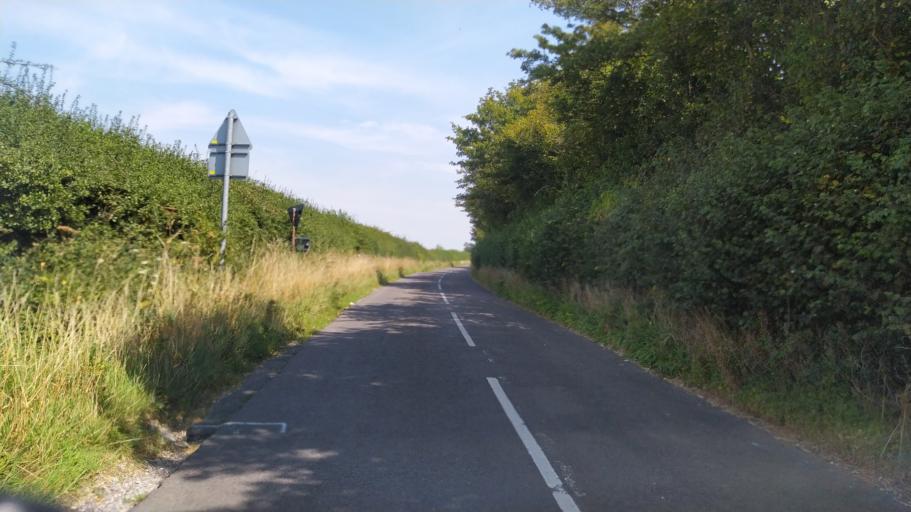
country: GB
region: England
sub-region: Hampshire
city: Cowplain
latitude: 50.9462
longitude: -1.0058
